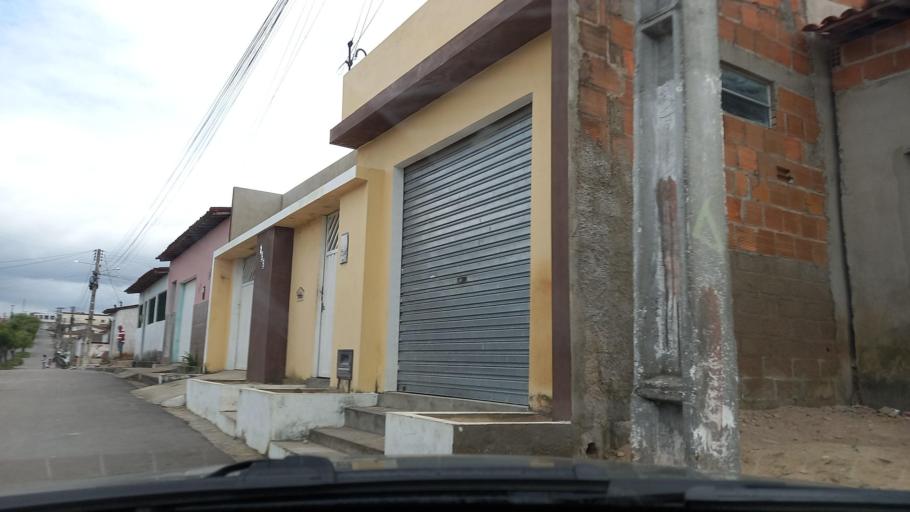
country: BR
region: Sergipe
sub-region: Caninde De Sao Francisco
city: Caninde de Sao Francisco
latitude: -9.6034
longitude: -37.7542
